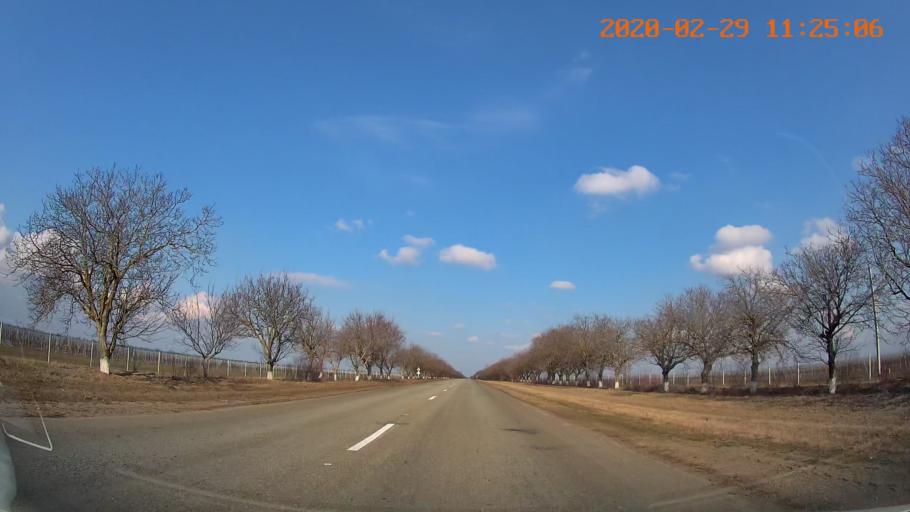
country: MD
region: Telenesti
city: Cocieri
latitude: 47.4338
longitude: 29.1518
